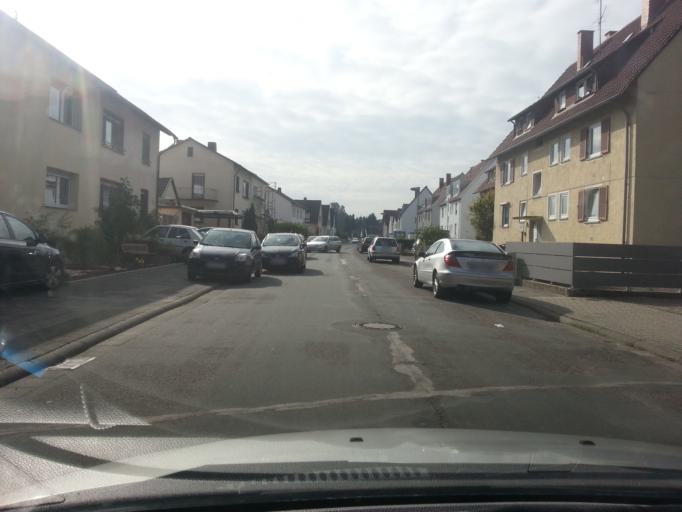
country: DE
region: Rheinland-Pfalz
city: Hassloch
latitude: 49.3513
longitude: 8.2556
